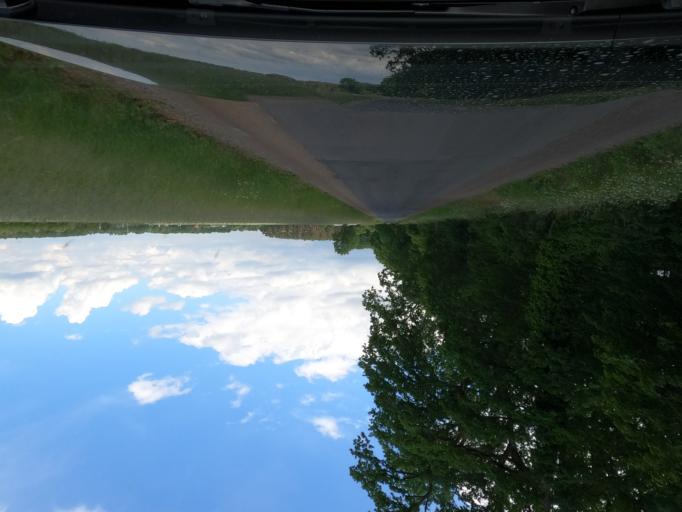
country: DE
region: Lower Saxony
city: Schwarmstedt
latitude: 52.6565
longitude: 9.6234
